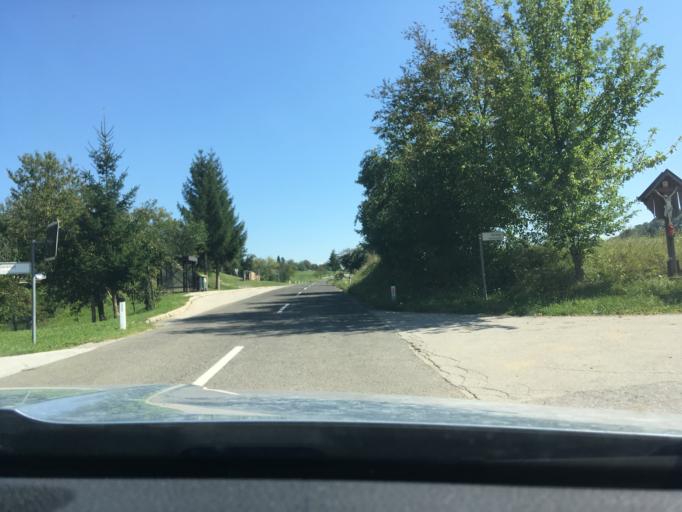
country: SI
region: Metlika
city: Metlika
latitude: 45.5152
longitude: 15.3201
